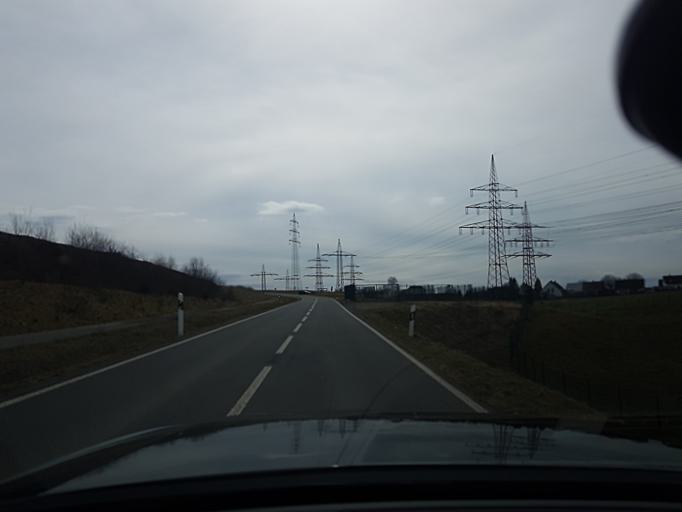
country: DE
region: North Rhine-Westphalia
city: Altena
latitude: 51.2522
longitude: 7.6834
